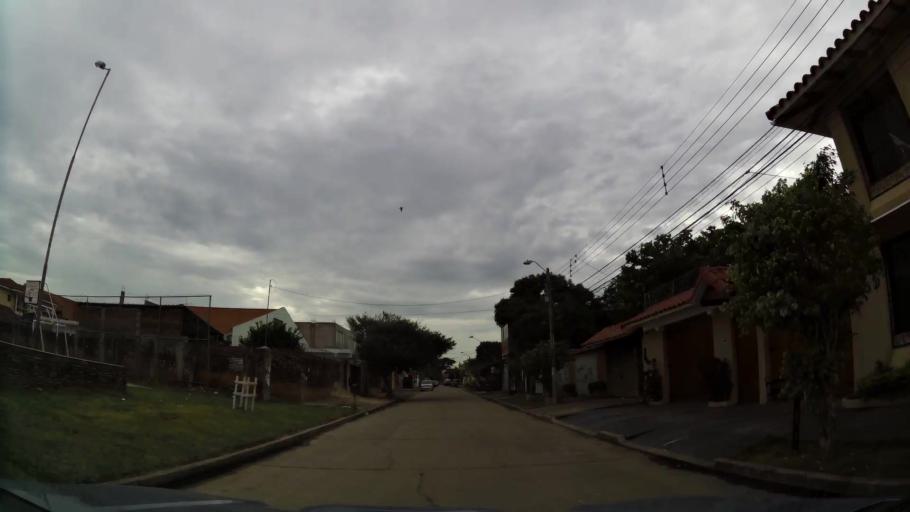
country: BO
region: Santa Cruz
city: Santa Cruz de la Sierra
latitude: -17.7705
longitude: -63.1591
